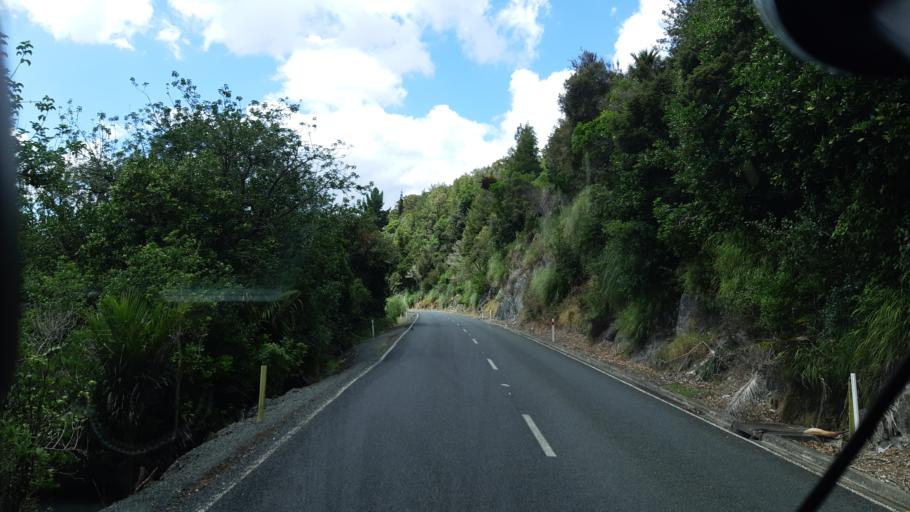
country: NZ
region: Northland
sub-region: Far North District
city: Taipa
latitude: -35.2518
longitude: 173.5323
